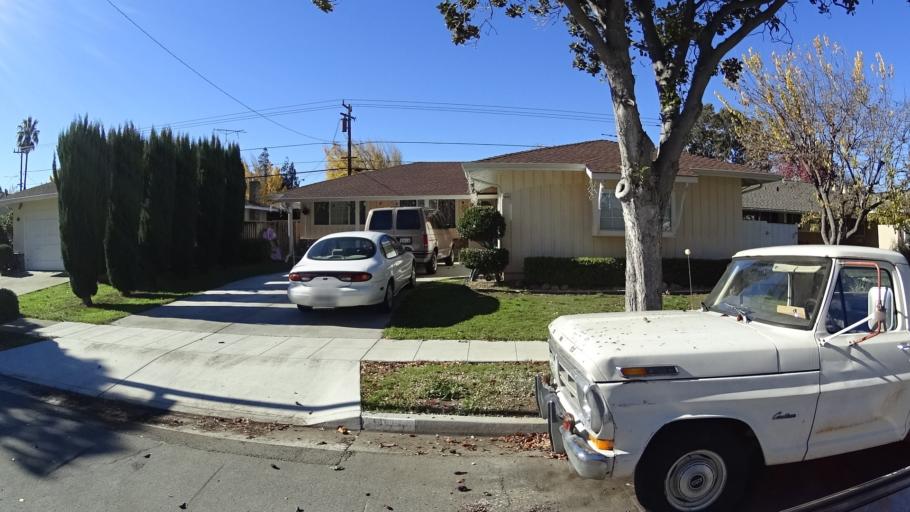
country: US
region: California
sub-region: Santa Clara County
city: Cupertino
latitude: 37.3405
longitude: -122.0046
